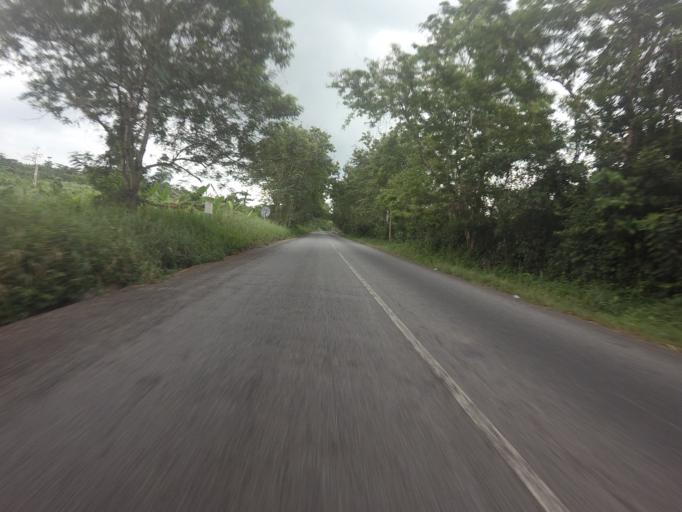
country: GH
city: Akropong
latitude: 5.9567
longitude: -0.1158
